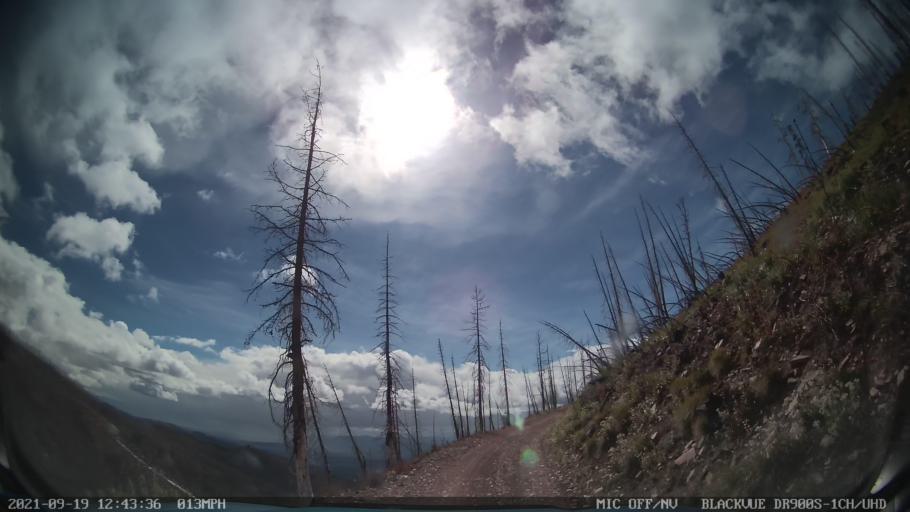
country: US
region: Montana
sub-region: Missoula County
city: Seeley Lake
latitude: 47.1900
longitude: -113.3468
